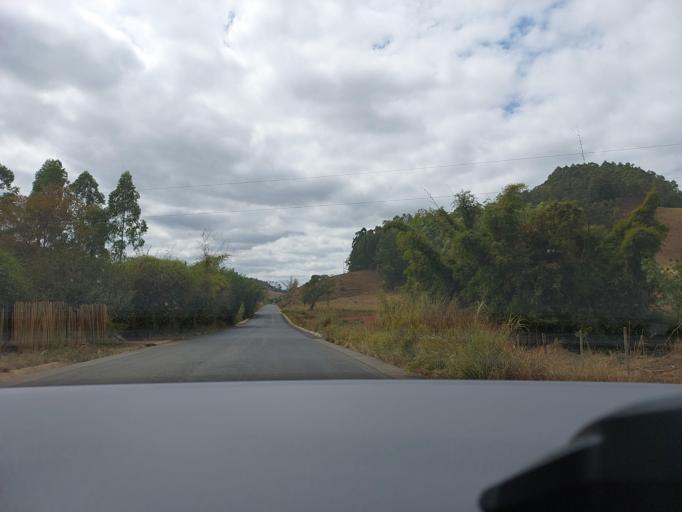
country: BR
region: Minas Gerais
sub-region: Vicosa
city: Vicosa
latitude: -20.8312
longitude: -42.7555
